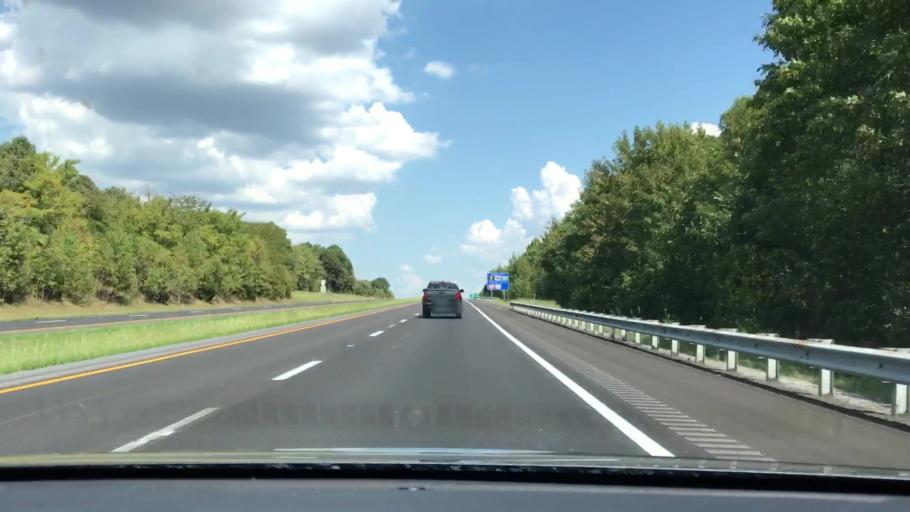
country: US
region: Kentucky
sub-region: Lyon County
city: Eddyville
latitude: 37.0986
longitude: -88.0400
